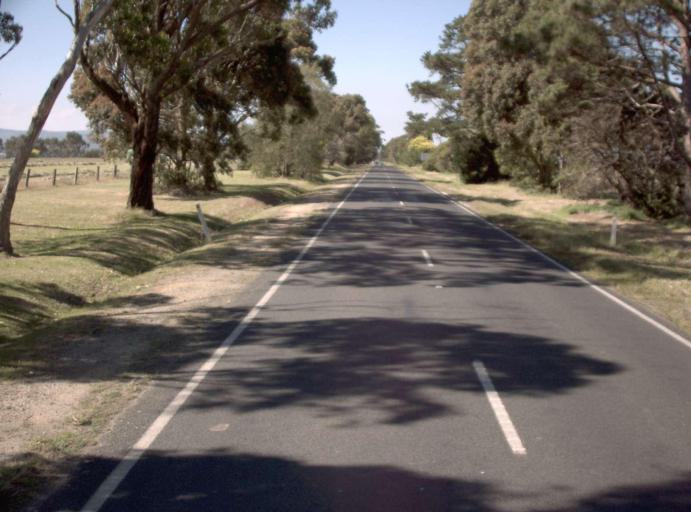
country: AU
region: Victoria
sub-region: Latrobe
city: Traralgon
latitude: -38.5867
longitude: 146.6708
